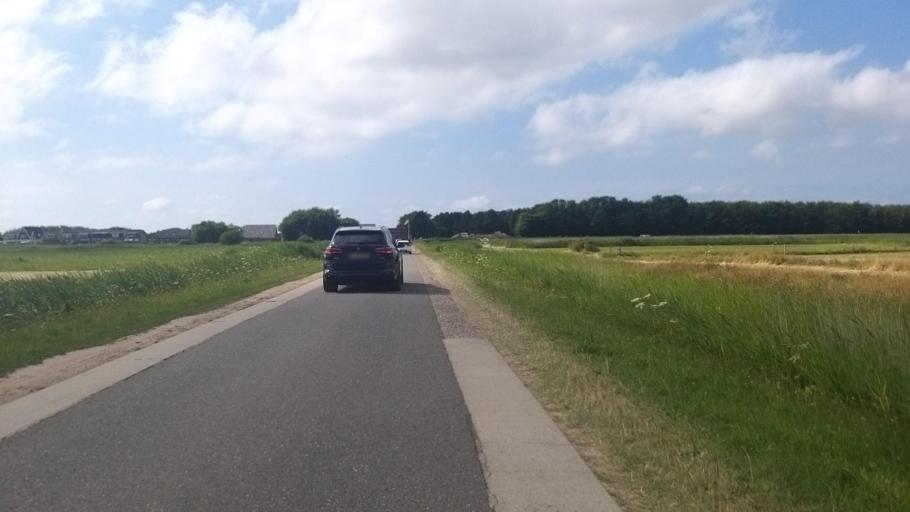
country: NL
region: North Holland
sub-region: Gemeente Texel
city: Den Burg
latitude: 53.1457
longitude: 4.8642
